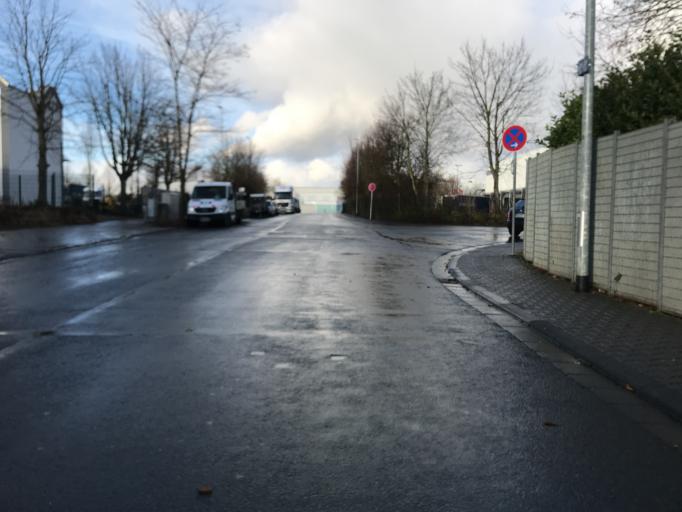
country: DE
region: Rheinland-Pfalz
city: Mainz
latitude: 49.9561
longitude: 8.2531
